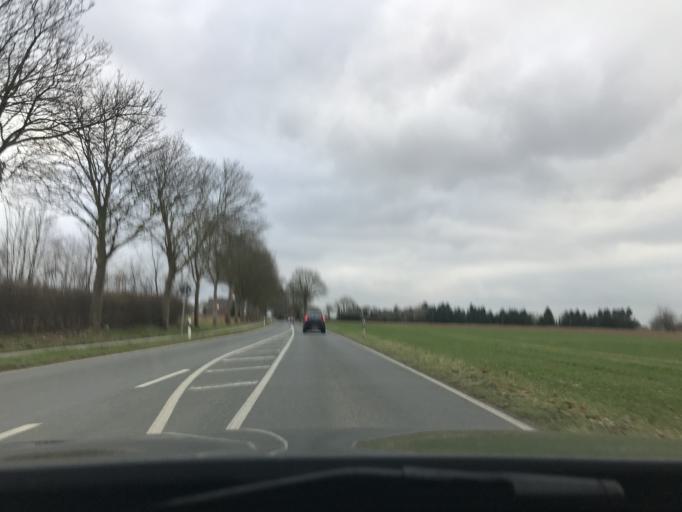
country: DE
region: North Rhine-Westphalia
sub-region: Regierungsbezirk Dusseldorf
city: Kleve
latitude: 51.7536
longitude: 6.1892
